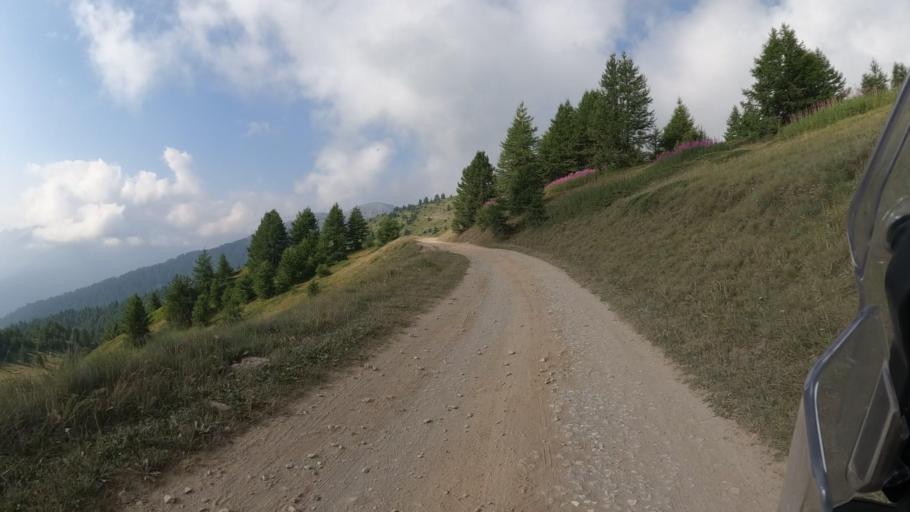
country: IT
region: Piedmont
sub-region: Provincia di Torino
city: Sauze d'Oulx
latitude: 45.0055
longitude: 6.8917
